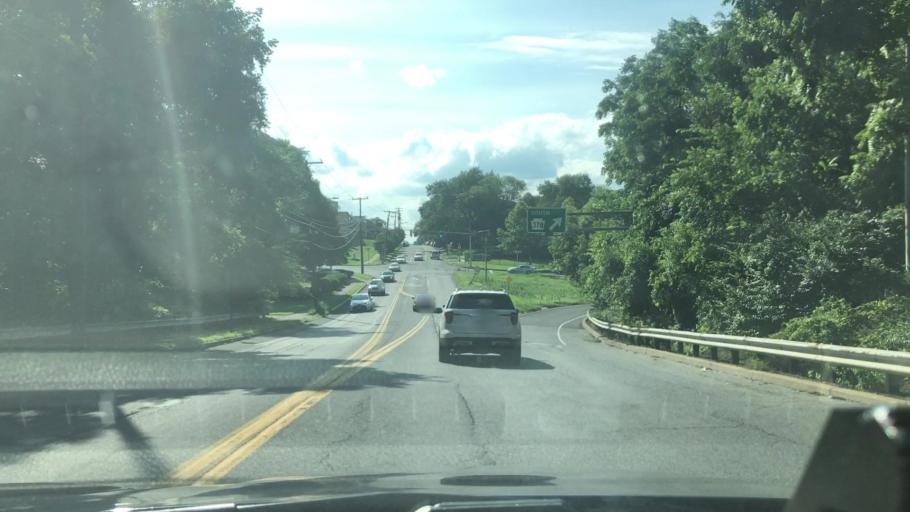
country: US
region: Pennsylvania
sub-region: Lehigh County
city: Fountain Hill
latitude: 40.6399
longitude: -75.4103
